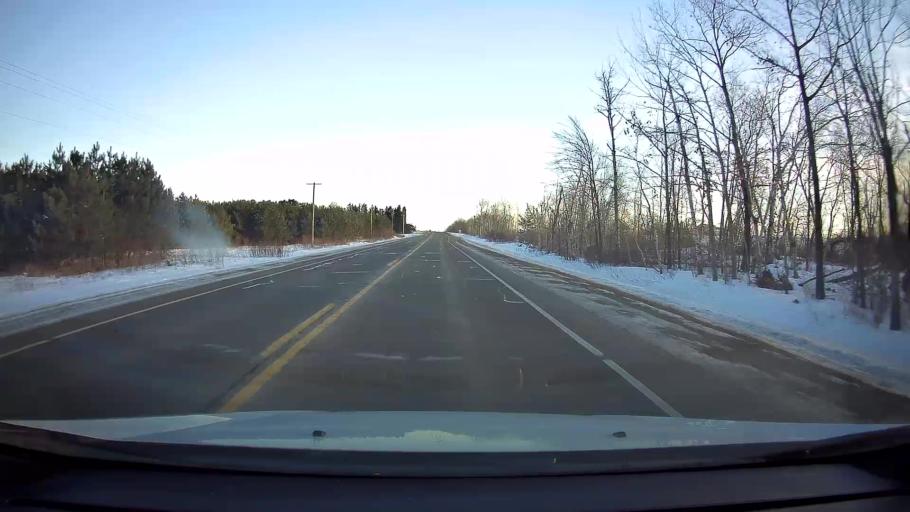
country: US
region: Wisconsin
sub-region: Barron County
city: Cumberland
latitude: 45.4849
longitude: -92.0654
